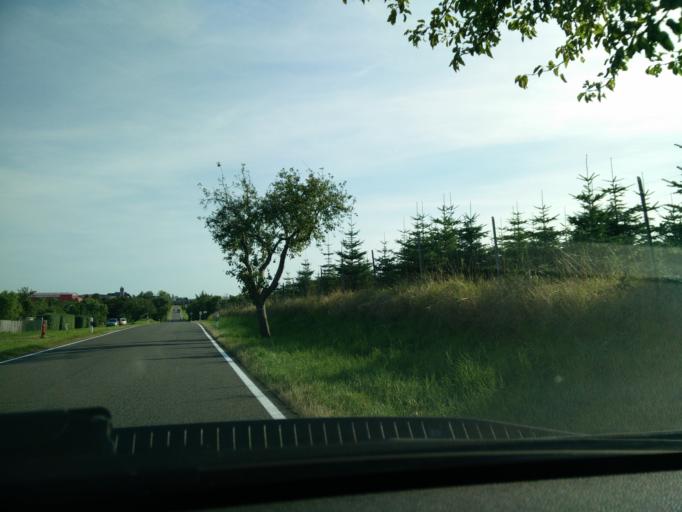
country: DE
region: Saxony
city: Geithain
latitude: 51.0693
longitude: 12.6905
